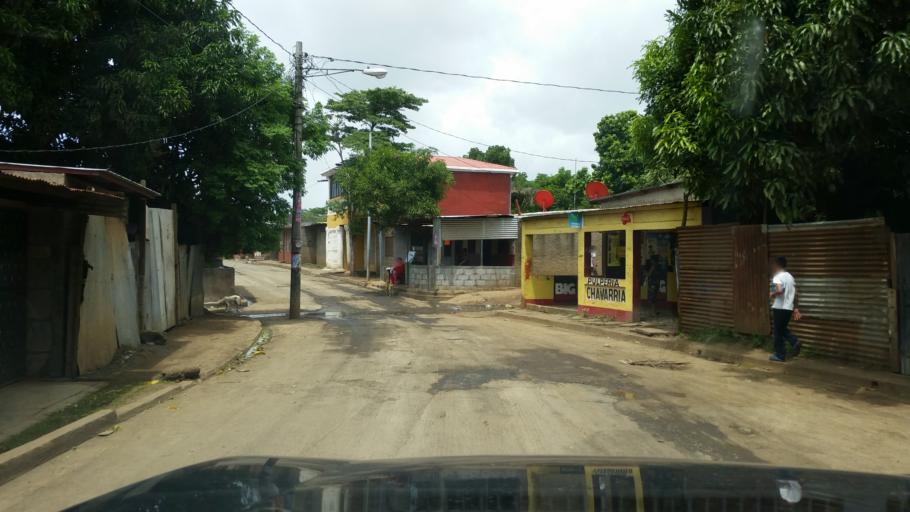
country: NI
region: Managua
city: Managua
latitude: 12.1131
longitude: -86.2212
